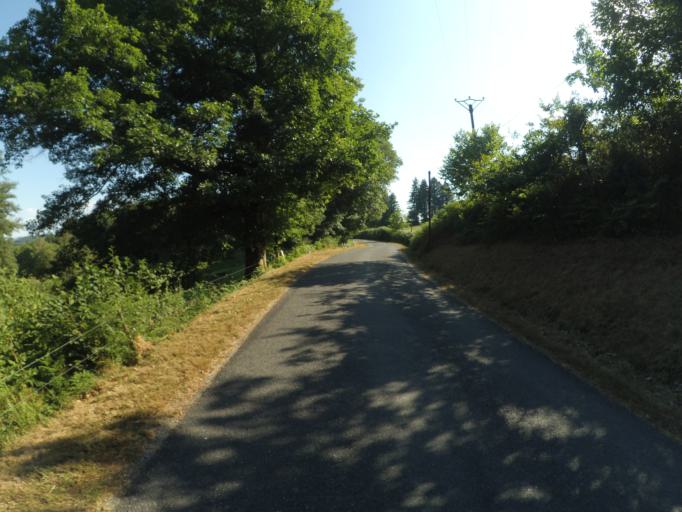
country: FR
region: Limousin
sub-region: Departement de la Haute-Vienne
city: Eymoutiers
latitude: 45.7303
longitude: 1.8226
